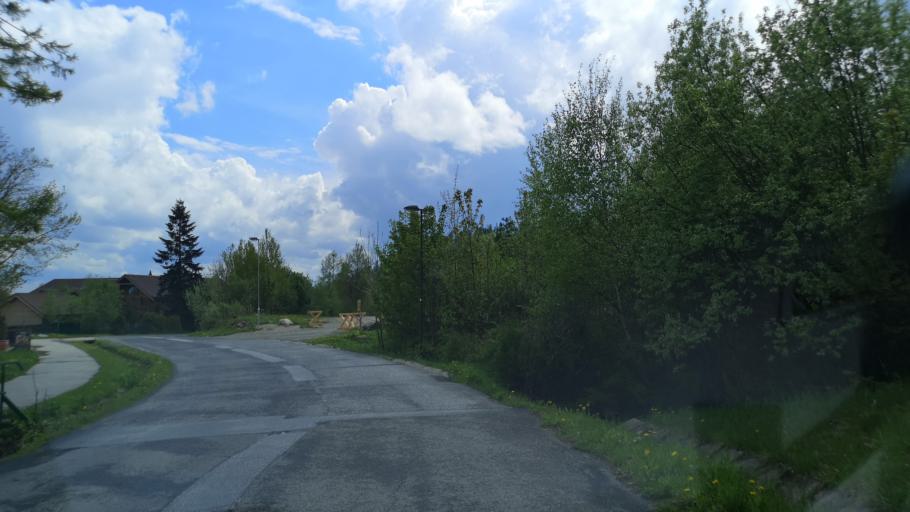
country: SK
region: Presovsky
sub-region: Okres Poprad
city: Vysoke Tatry
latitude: 49.1658
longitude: 20.2722
